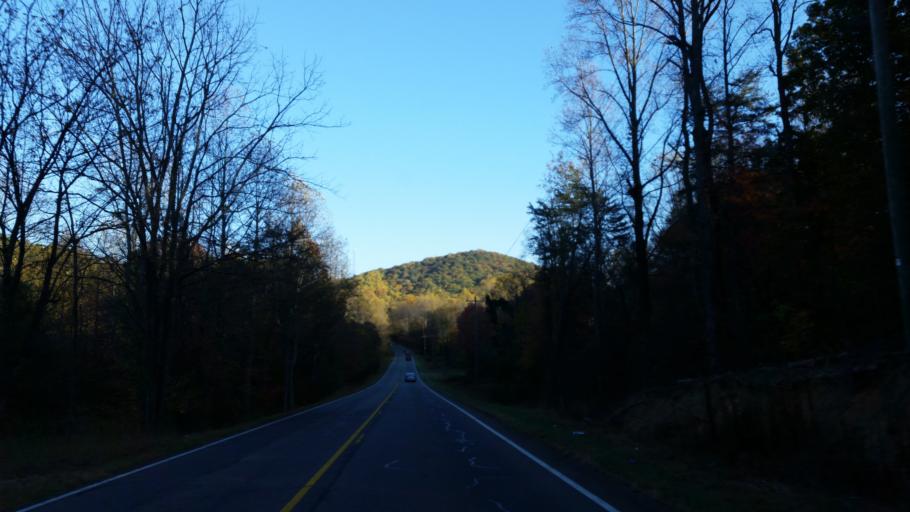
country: US
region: Georgia
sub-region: Pickens County
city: Jasper
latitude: 34.5941
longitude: -84.3243
